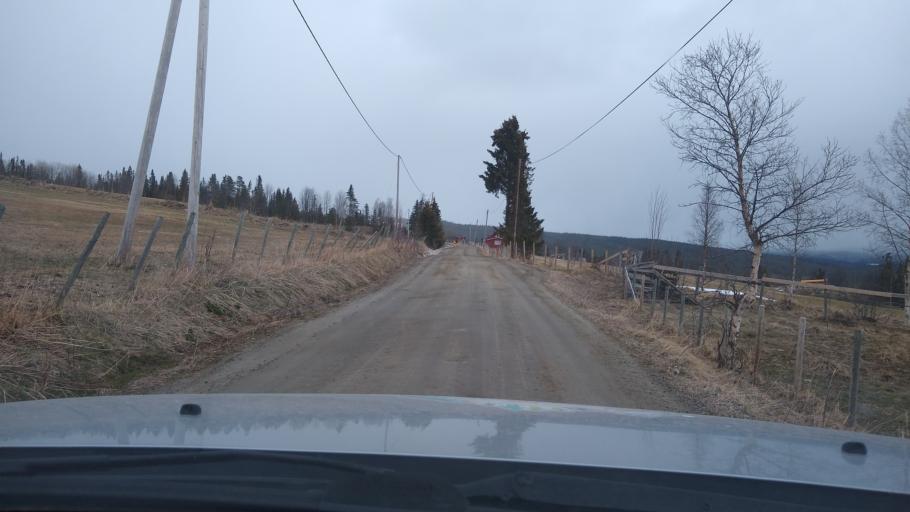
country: NO
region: Oppland
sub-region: Oyer
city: Tretten
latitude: 61.4603
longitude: 10.3331
